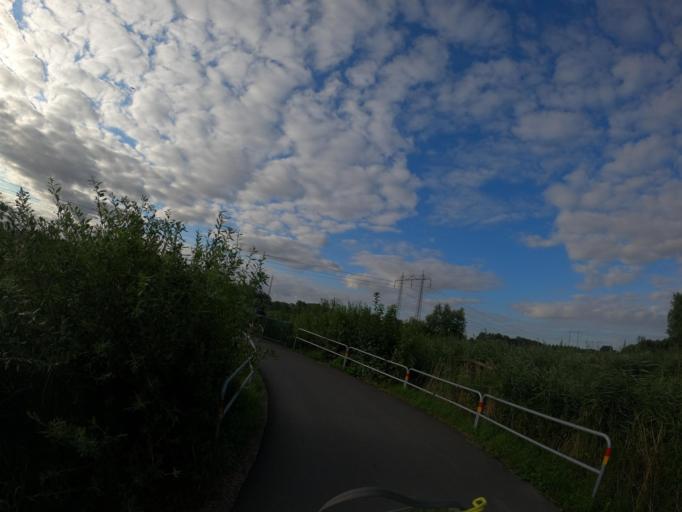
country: SE
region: Skane
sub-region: Staffanstorps Kommun
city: Staffanstorp
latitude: 55.6586
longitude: 13.2117
